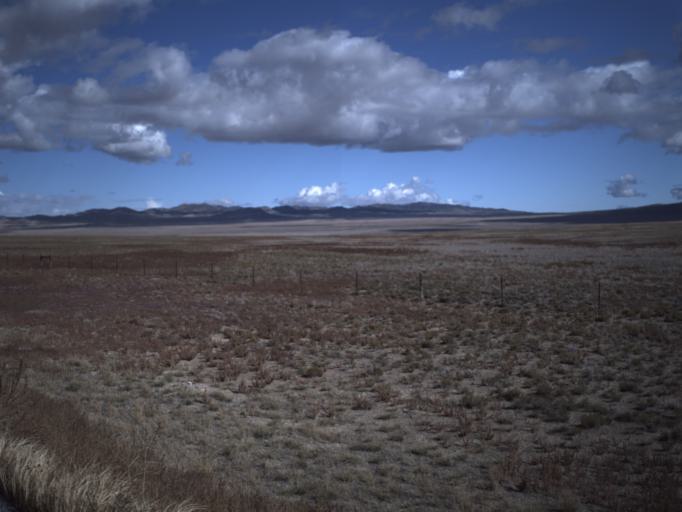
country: US
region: Utah
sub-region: Beaver County
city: Milford
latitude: 38.6366
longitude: -113.8584
